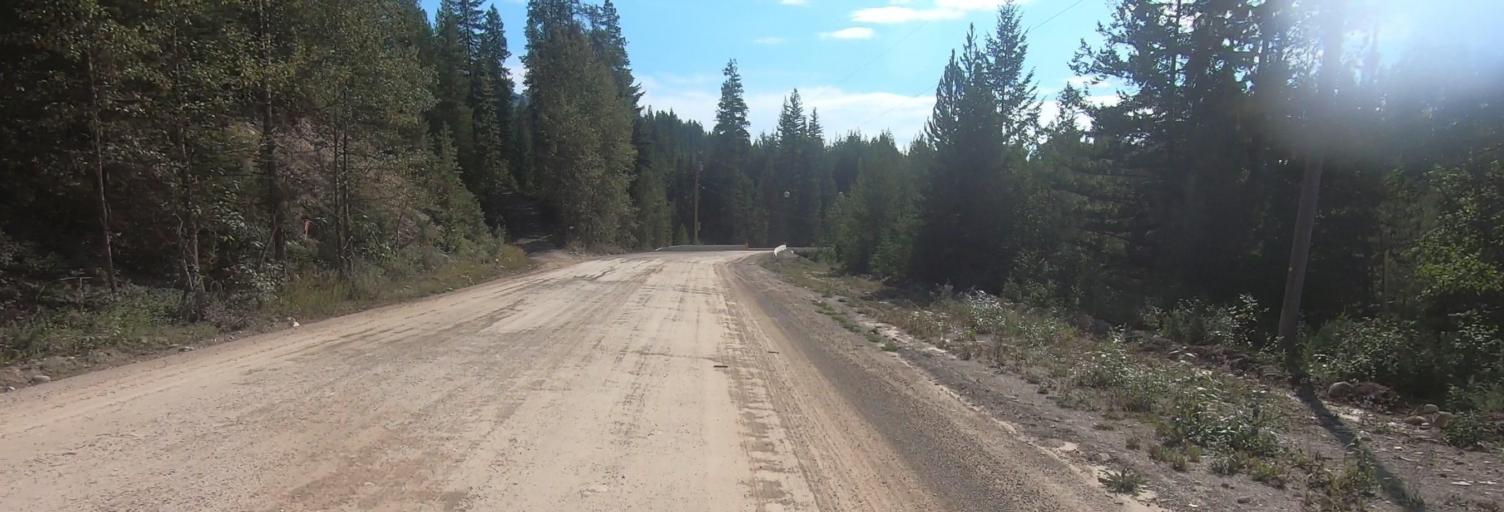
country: CA
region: British Columbia
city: Golden
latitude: 51.4997
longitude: -117.1774
